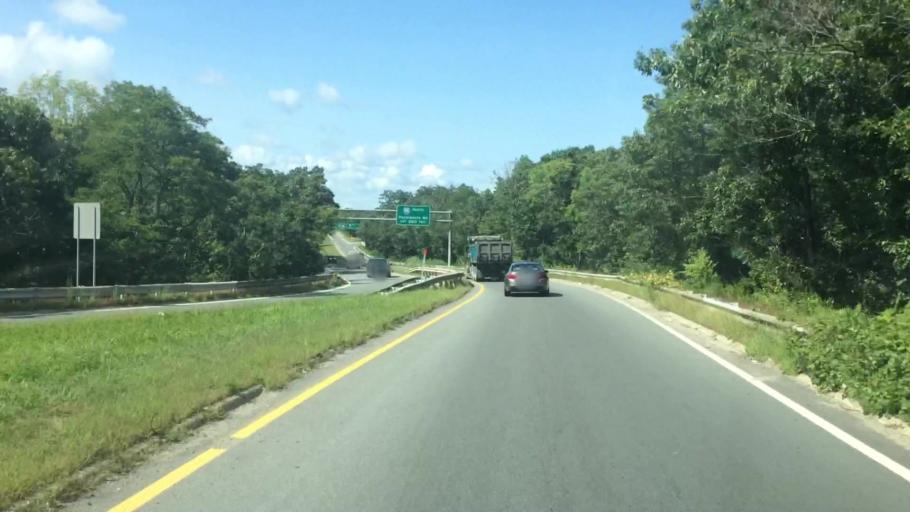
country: US
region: Massachusetts
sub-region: Essex County
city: South Peabody
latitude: 42.5138
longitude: -70.9909
